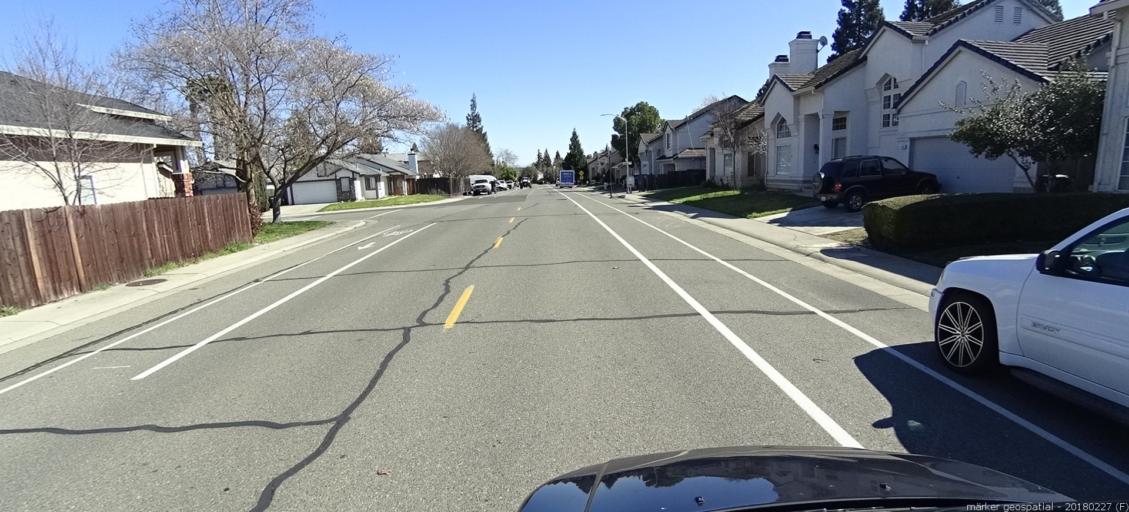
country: US
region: California
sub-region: Sacramento County
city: North Highlands
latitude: 38.7257
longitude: -121.3822
